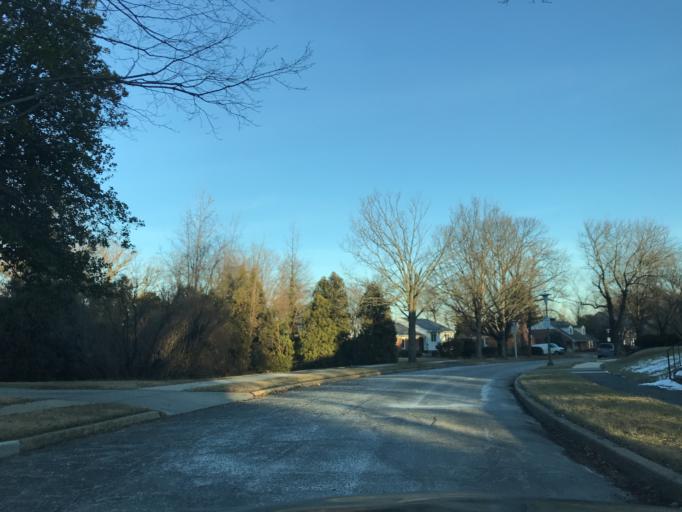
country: US
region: Maryland
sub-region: Baltimore County
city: Towson
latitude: 39.3474
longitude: -76.6146
